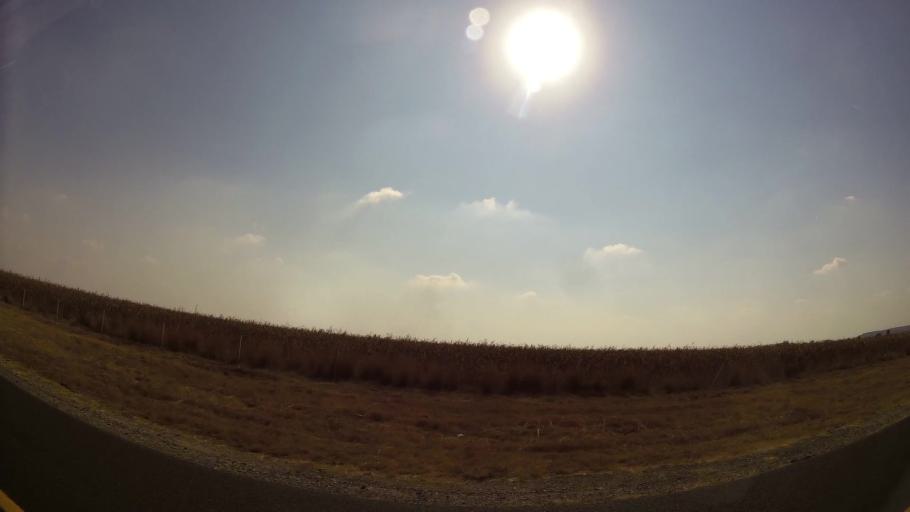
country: ZA
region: Gauteng
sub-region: Ekurhuleni Metropolitan Municipality
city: Springs
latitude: -26.1642
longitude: 28.4875
